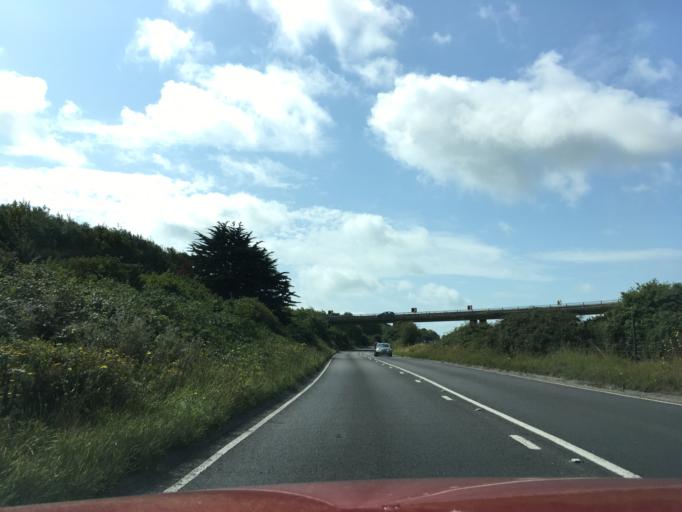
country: GB
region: England
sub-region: West Sussex
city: Shoreham-by-Sea
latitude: 50.8446
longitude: -0.2849
